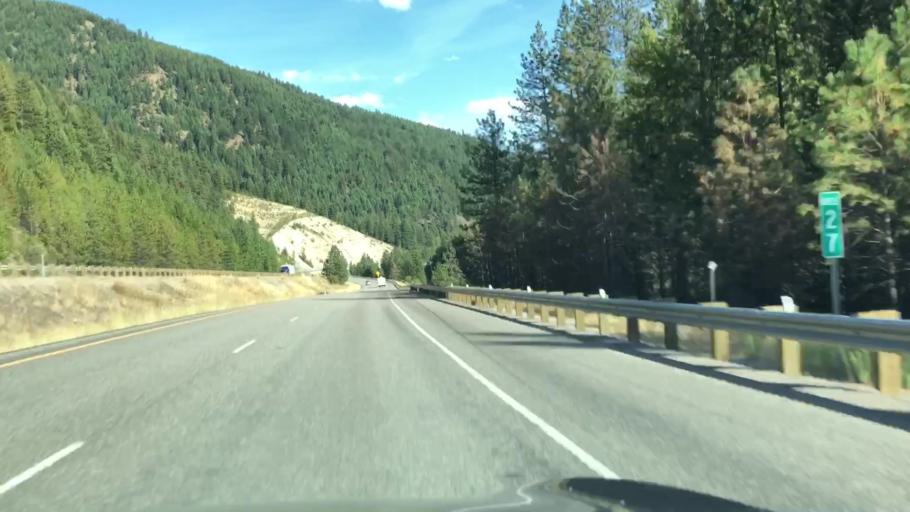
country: US
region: Montana
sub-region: Sanders County
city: Thompson Falls
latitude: 47.3133
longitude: -115.2205
